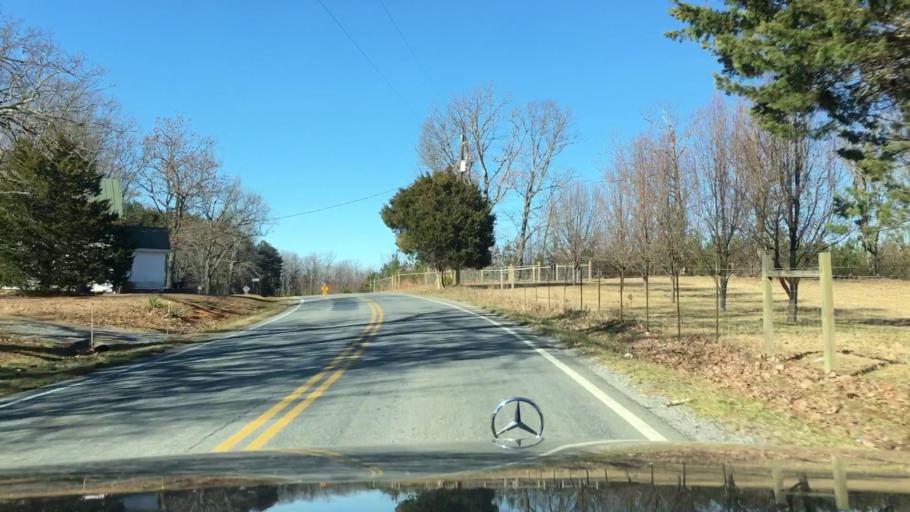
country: US
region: Virginia
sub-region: Pittsylvania County
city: Motley
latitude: 37.1644
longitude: -79.4035
